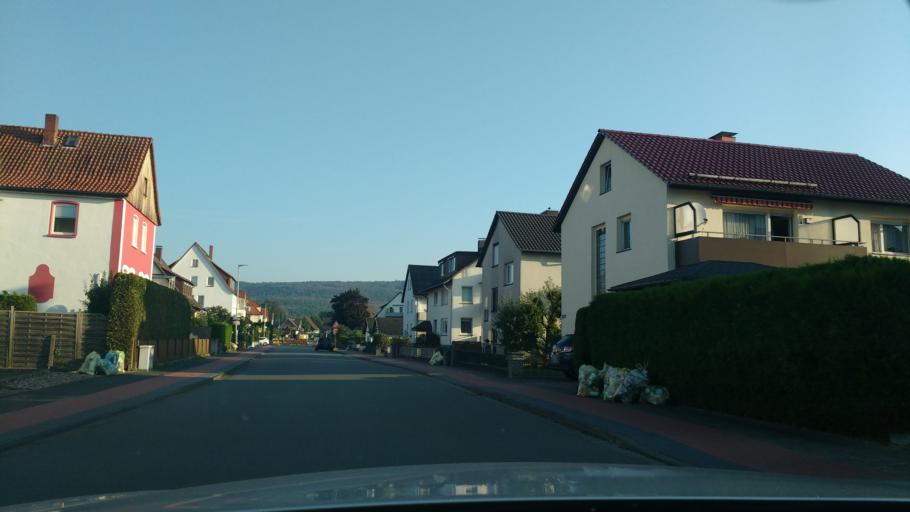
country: DE
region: Lower Saxony
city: Bad Pyrmont
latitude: 51.9822
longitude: 9.2310
